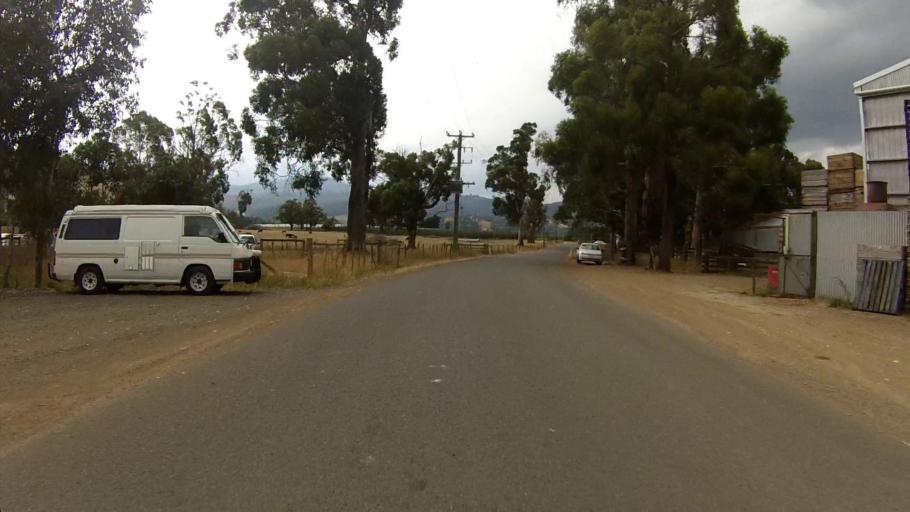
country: AU
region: Tasmania
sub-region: Huon Valley
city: Huonville
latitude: -42.9944
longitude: 147.0626
